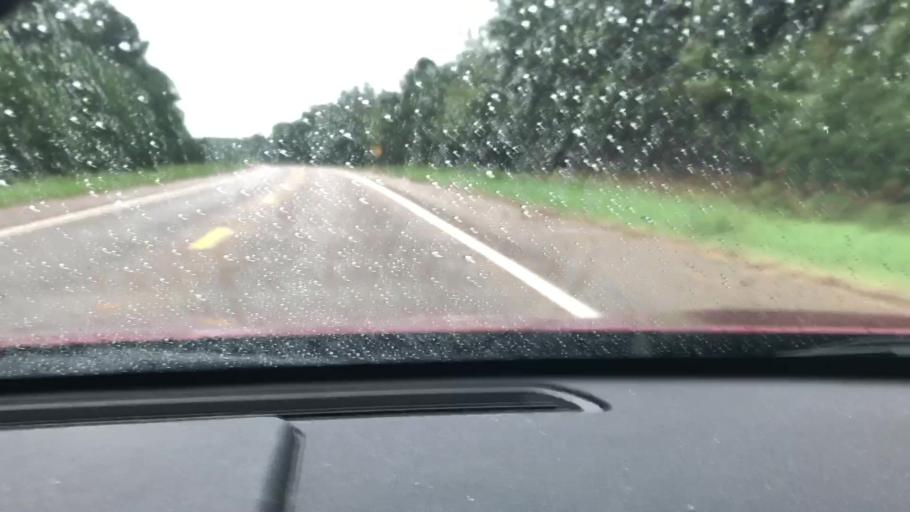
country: US
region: Arkansas
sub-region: Columbia County
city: Magnolia
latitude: 33.2977
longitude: -93.2613
